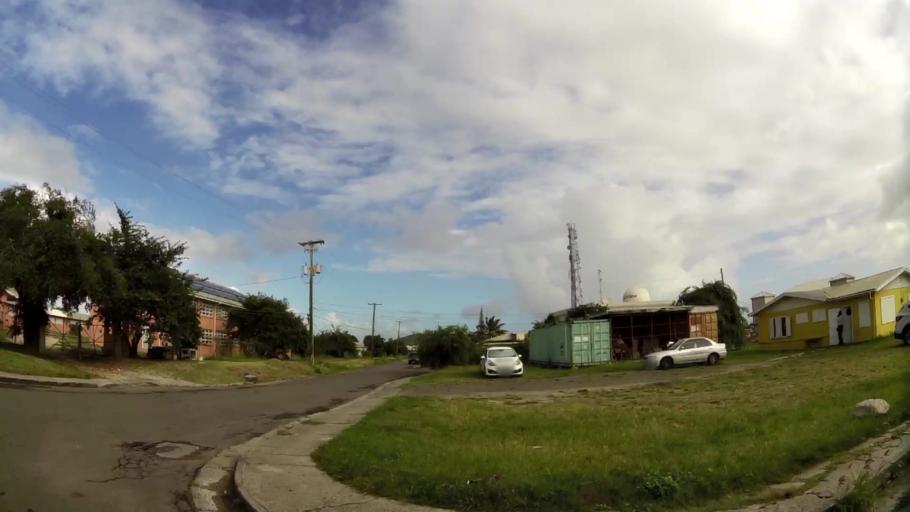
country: AG
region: Saint John
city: Saint John's
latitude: 17.1267
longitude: -61.8228
